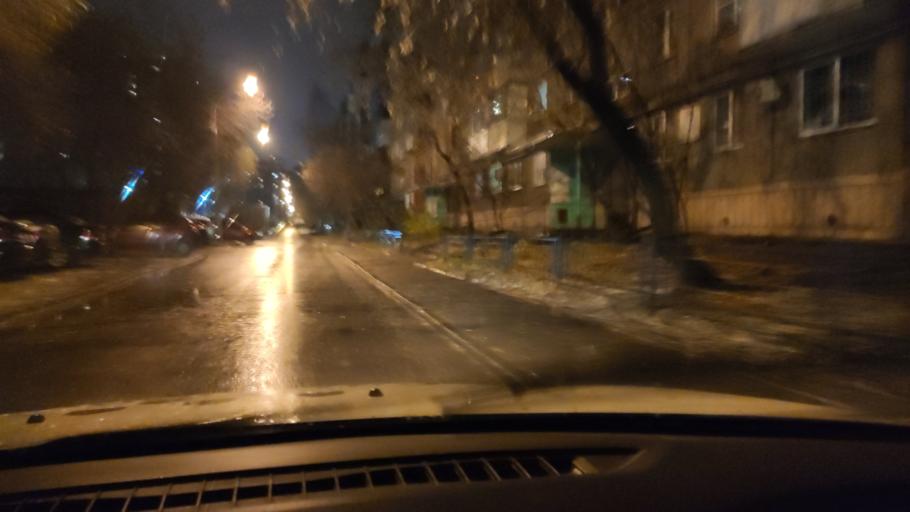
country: RU
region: Perm
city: Kondratovo
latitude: 57.9985
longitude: 56.1483
